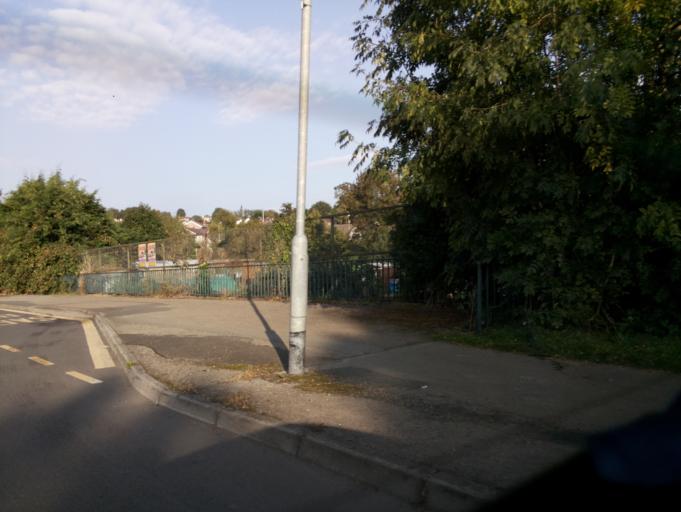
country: GB
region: Wales
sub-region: Torfaen County Borough
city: Cwmbran
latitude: 51.6586
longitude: -3.0132
